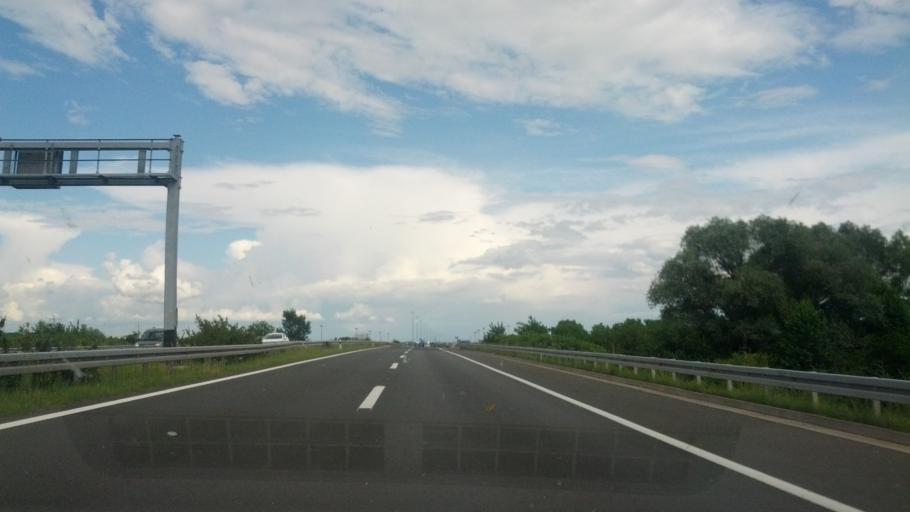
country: HR
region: Zagrebacka
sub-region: Grad Samobor
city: Samobor
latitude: 45.8291
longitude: 15.7305
